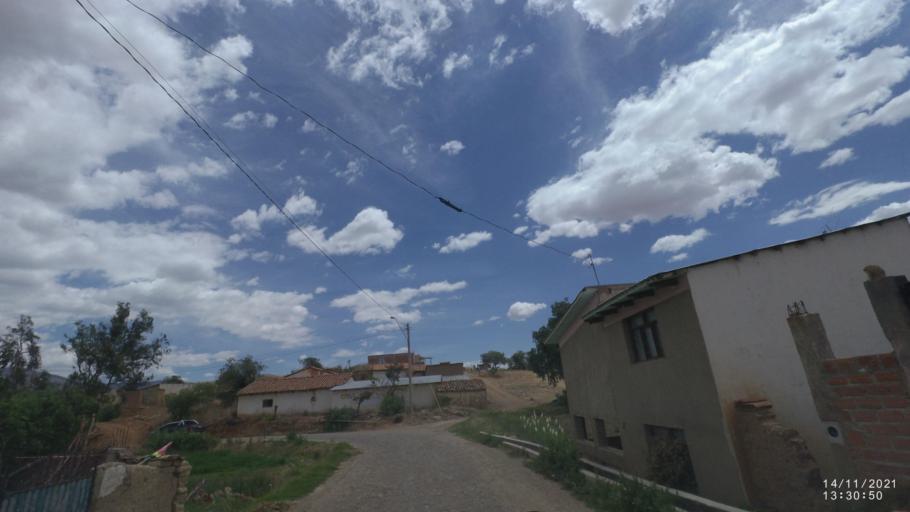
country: BO
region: Cochabamba
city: Colomi
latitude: -17.3932
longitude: -65.9817
